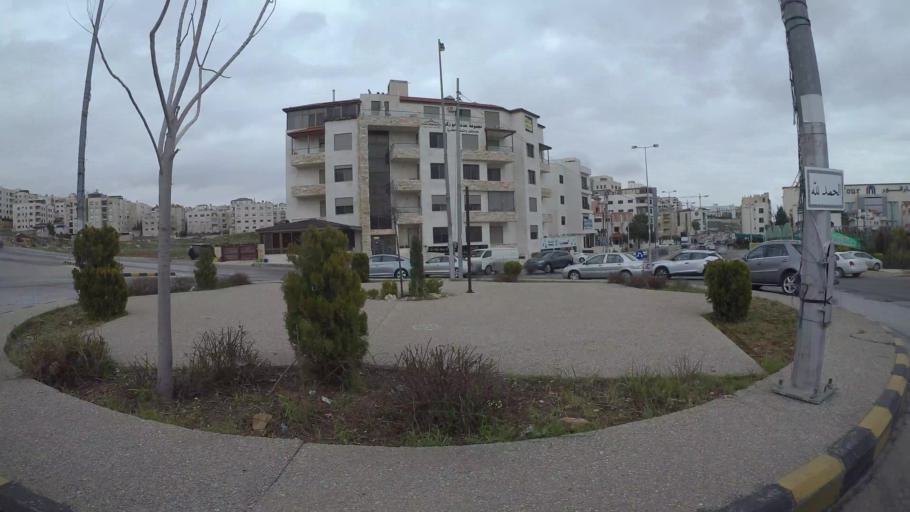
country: JO
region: Amman
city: Wadi as Sir
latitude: 31.9834
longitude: 35.8378
